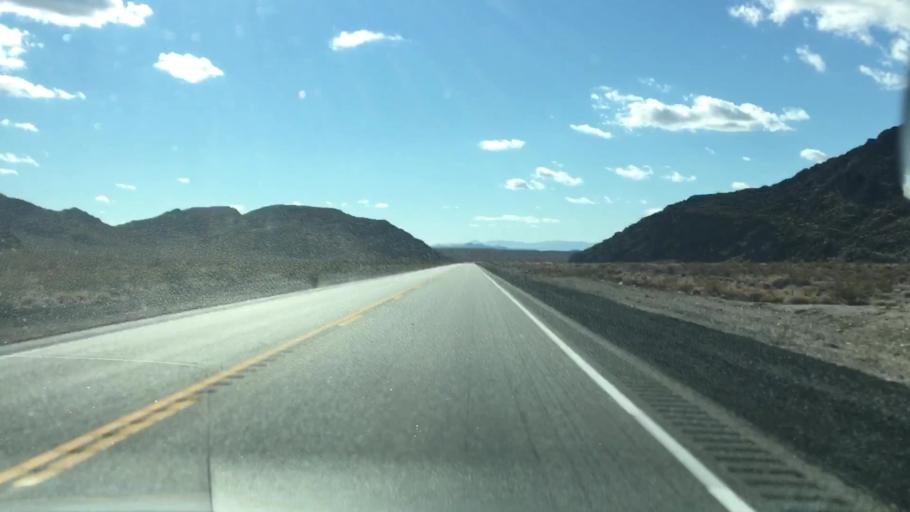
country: US
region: Nevada
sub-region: Nye County
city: Pahrump
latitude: 36.5722
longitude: -116.0761
